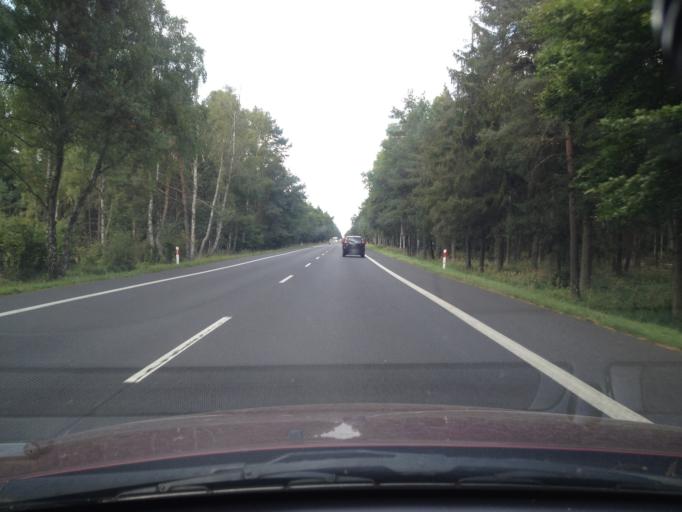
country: PL
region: West Pomeranian Voivodeship
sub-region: Powiat goleniowski
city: Goleniow
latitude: 53.6364
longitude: 14.8176
